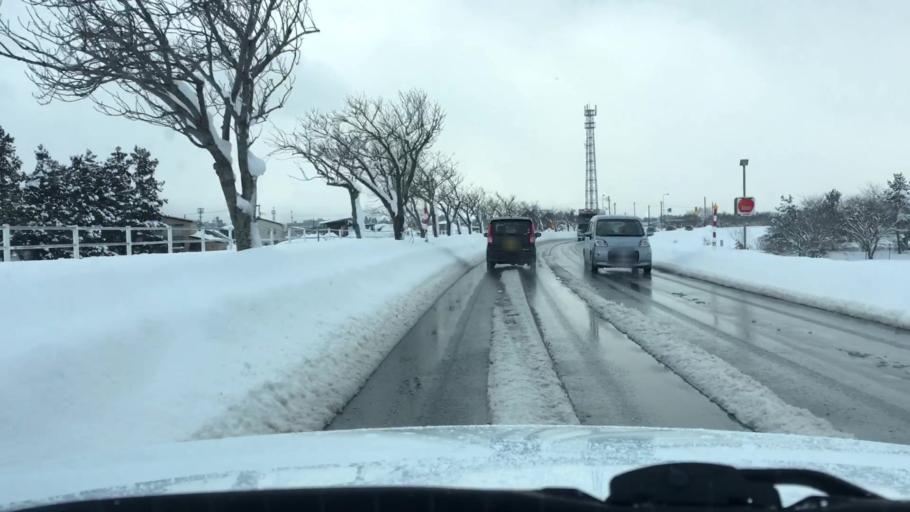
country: JP
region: Aomori
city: Hirosaki
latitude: 40.6235
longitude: 140.4731
